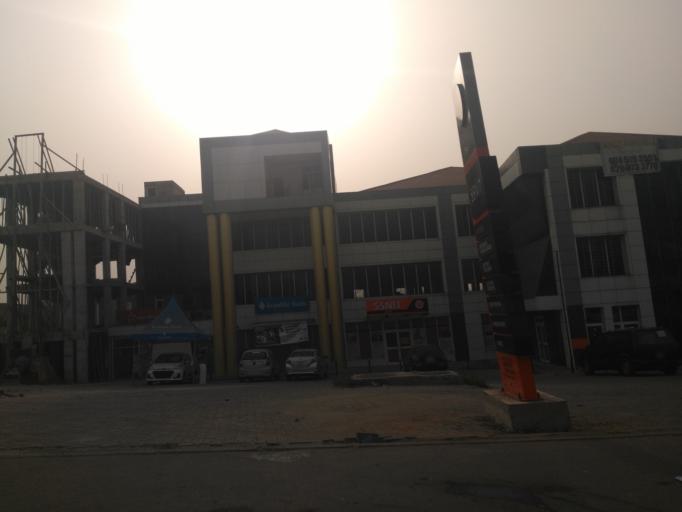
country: GH
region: Ashanti
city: Tafo
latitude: 6.7183
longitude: -1.6312
